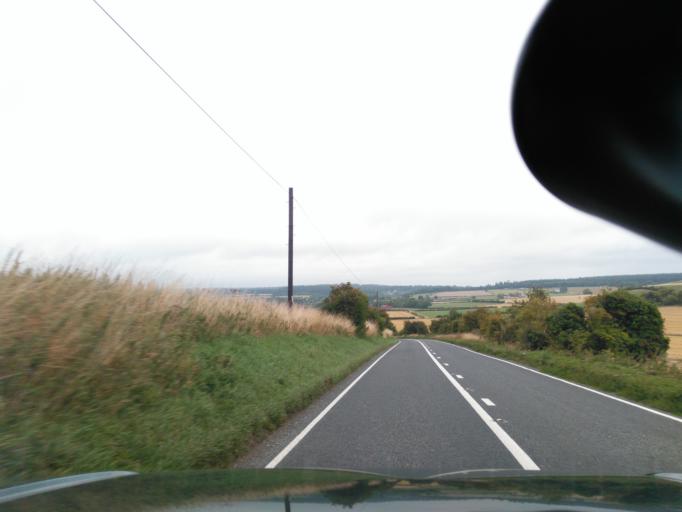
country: GB
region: England
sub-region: Wiltshire
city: Bishopstrow
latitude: 51.1550
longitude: -2.1713
